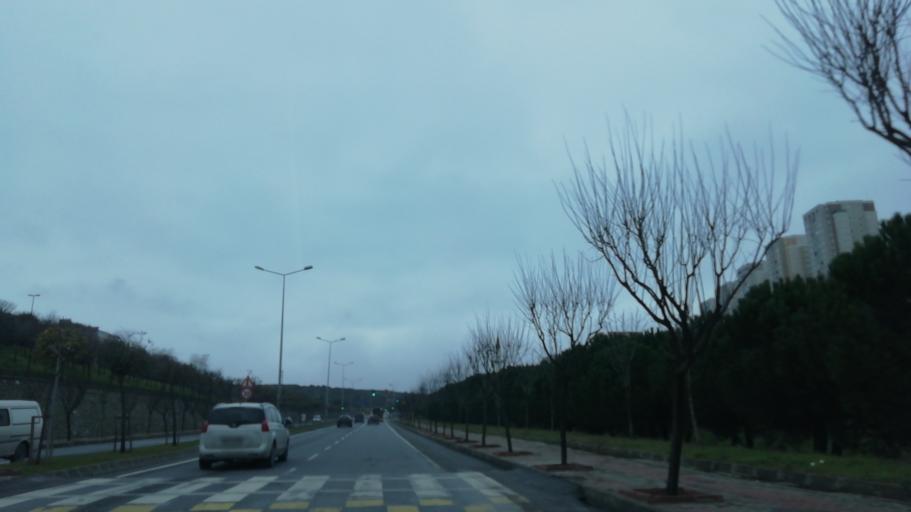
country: TR
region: Istanbul
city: Basaksehir
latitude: 41.1027
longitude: 28.8003
